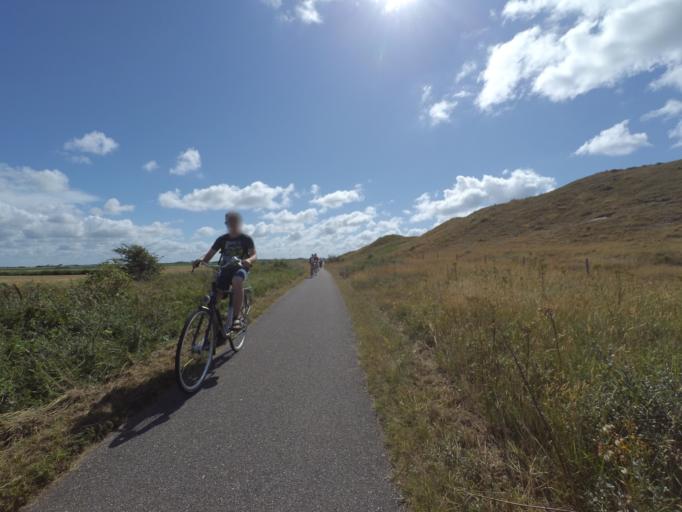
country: NL
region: North Holland
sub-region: Gemeente Texel
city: Den Burg
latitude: 53.1224
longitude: 4.8066
